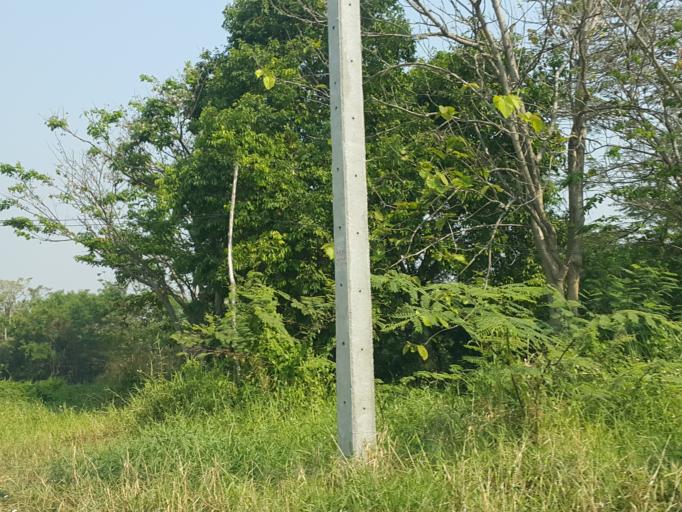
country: TH
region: Chiang Mai
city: Hang Dong
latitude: 18.7143
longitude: 98.9649
